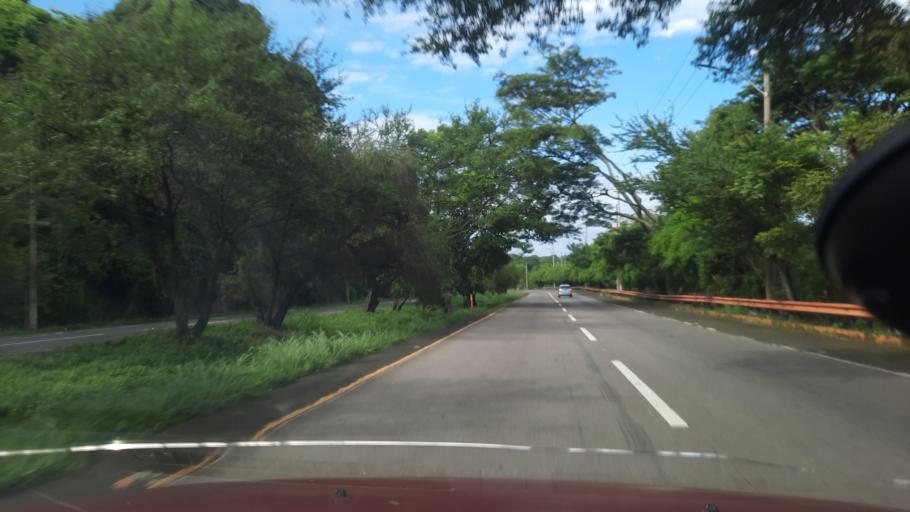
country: SV
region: La Paz
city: Olocuilta
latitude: 13.5322
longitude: -89.1133
